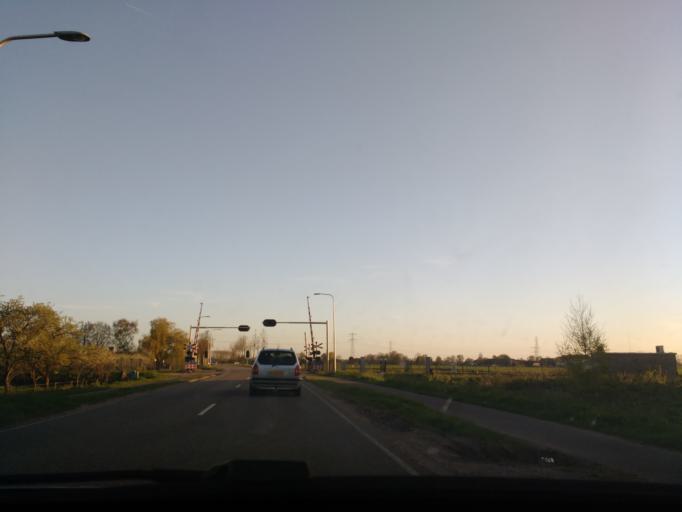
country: NL
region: Gelderland
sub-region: Gemeente Overbetuwe
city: Elst
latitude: 51.9038
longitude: 5.8382
